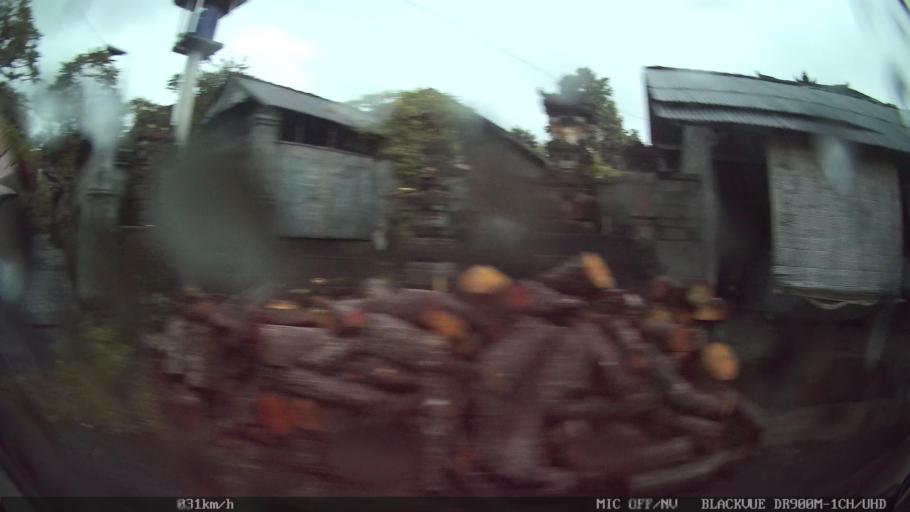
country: ID
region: Bali
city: Banjar Sedang
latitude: -8.5699
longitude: 115.2545
